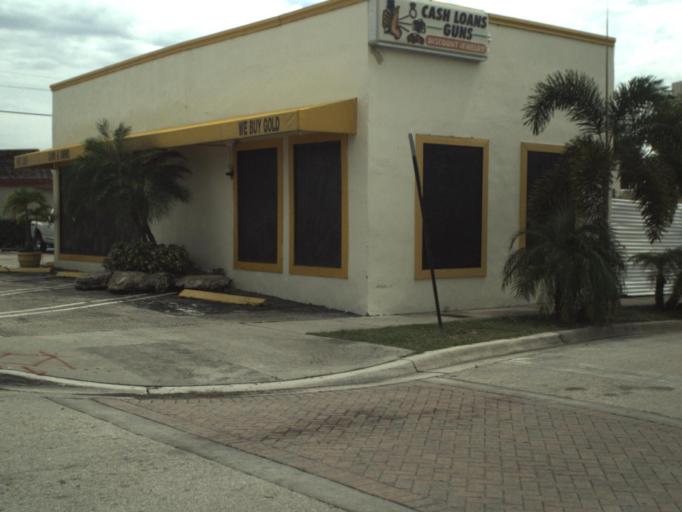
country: US
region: Florida
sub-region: Palm Beach County
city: Mangonia Park
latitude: 26.7550
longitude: -80.0559
